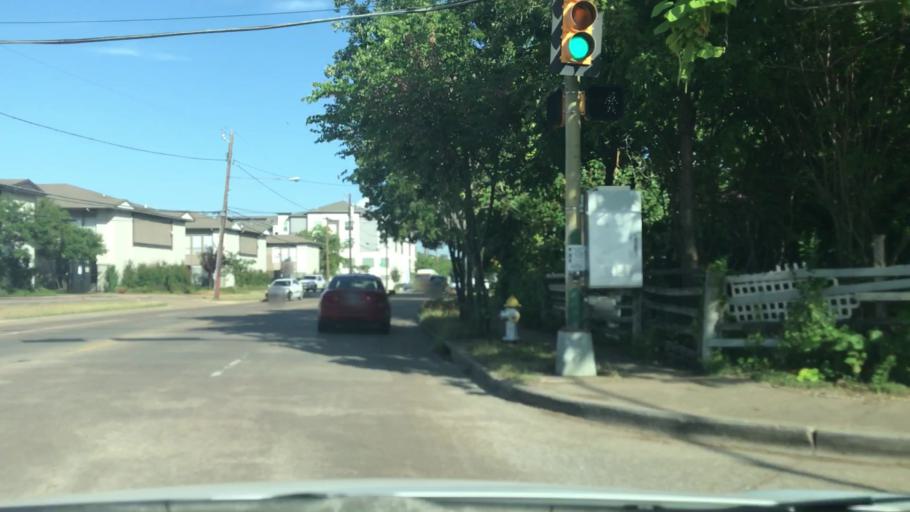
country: US
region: Texas
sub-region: Dallas County
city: Highland Park
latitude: 32.8229
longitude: -96.8274
